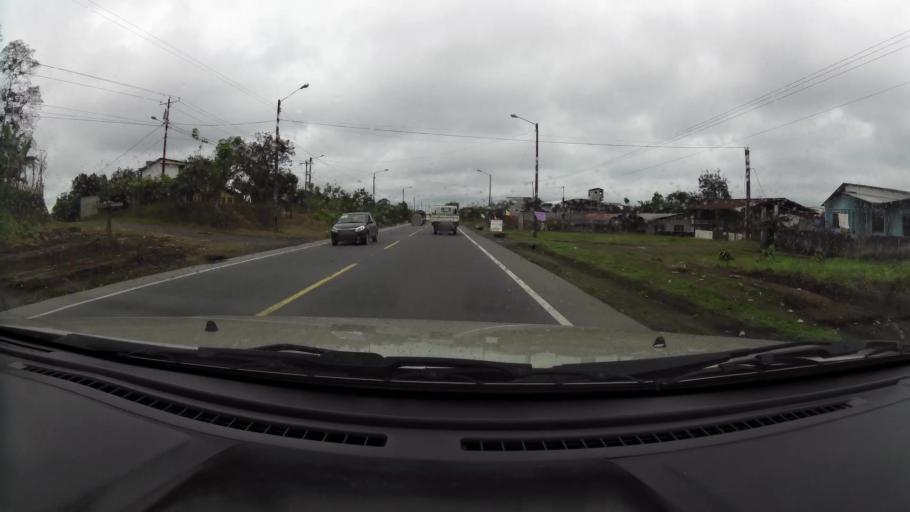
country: EC
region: Santo Domingo de los Tsachilas
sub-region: Canton Santo Domingo de los Colorados
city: Santo Domingo de los Colorados
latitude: -0.2763
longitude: -79.1695
